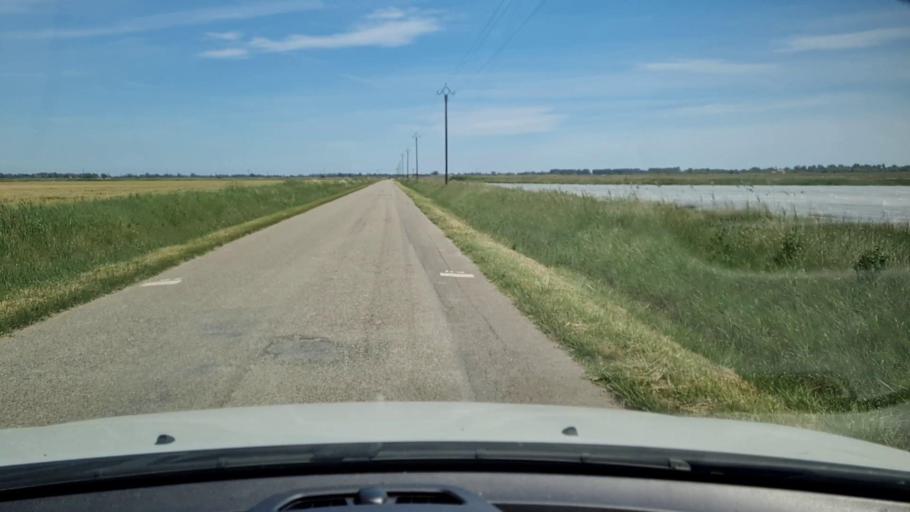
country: FR
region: Languedoc-Roussillon
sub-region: Departement du Gard
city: Saint-Gilles
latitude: 43.6081
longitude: 4.4312
